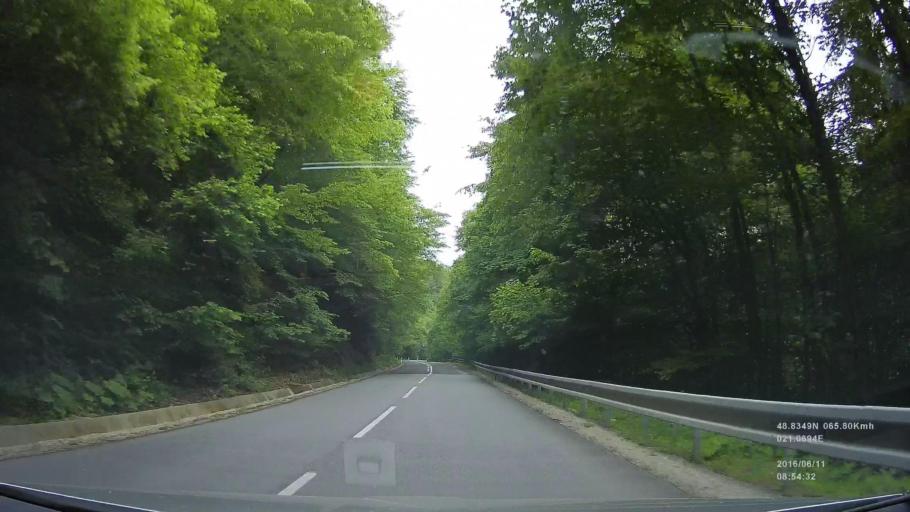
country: SK
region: Kosicky
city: Gelnica
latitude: 48.8032
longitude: 21.1026
